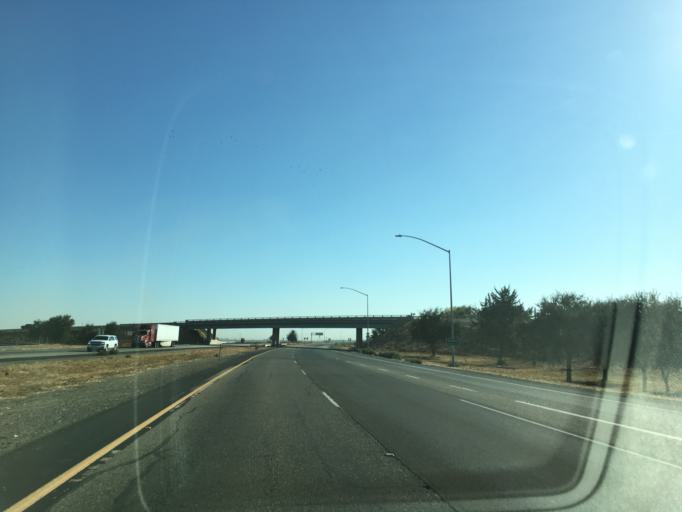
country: US
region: California
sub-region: Merced County
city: Dos Palos
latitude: 37.0826
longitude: -120.4949
